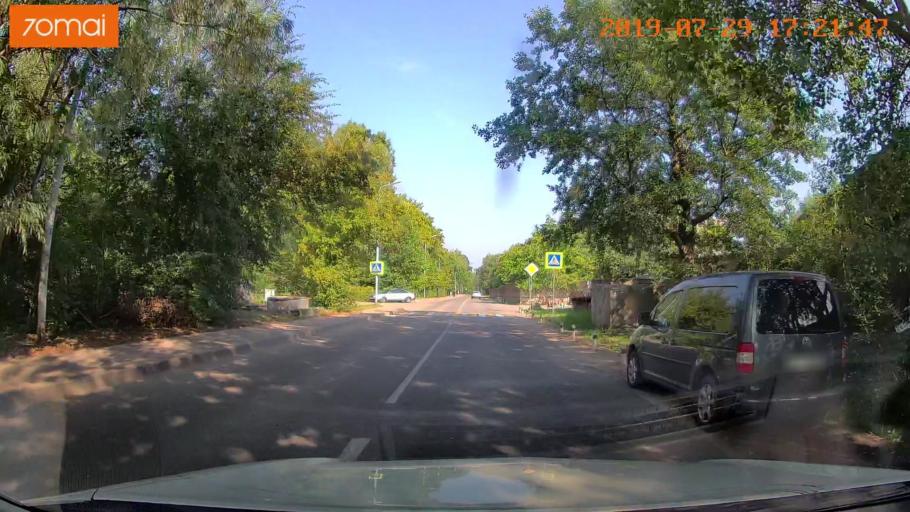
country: RU
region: Kaliningrad
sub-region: Gorod Kaliningrad
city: Kaliningrad
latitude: 54.7702
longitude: 20.4335
